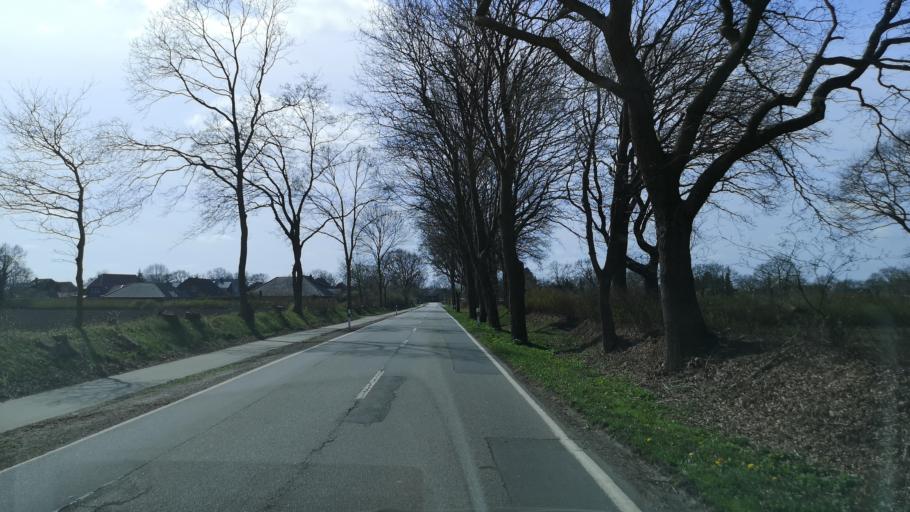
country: DE
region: Schleswig-Holstein
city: Tetenhusen
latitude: 54.3558
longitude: 9.5030
